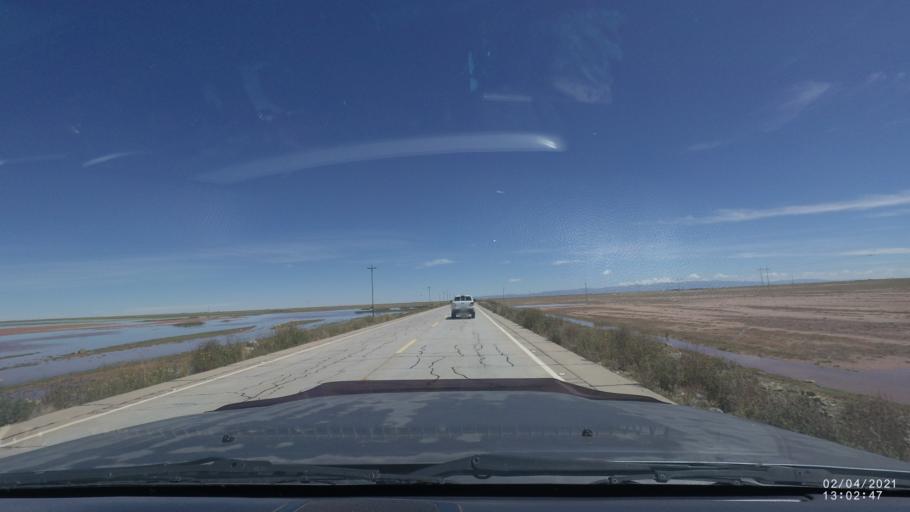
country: BO
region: Oruro
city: Oruro
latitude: -18.0513
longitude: -67.1865
